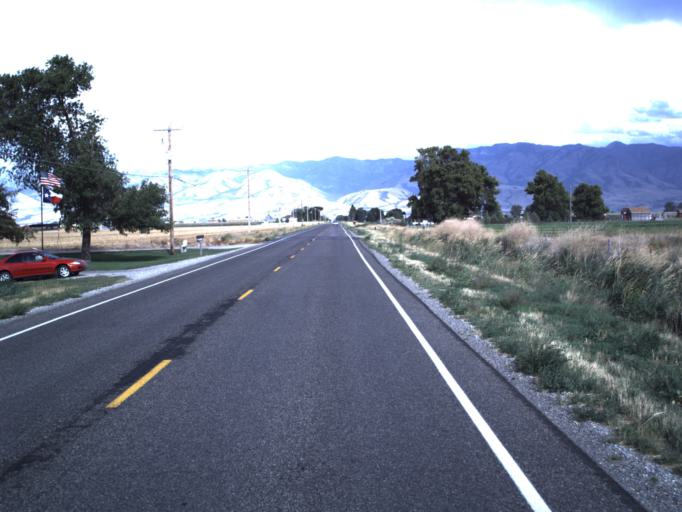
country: US
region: Utah
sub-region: Cache County
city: Lewiston
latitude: 41.9754
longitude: -111.9259
